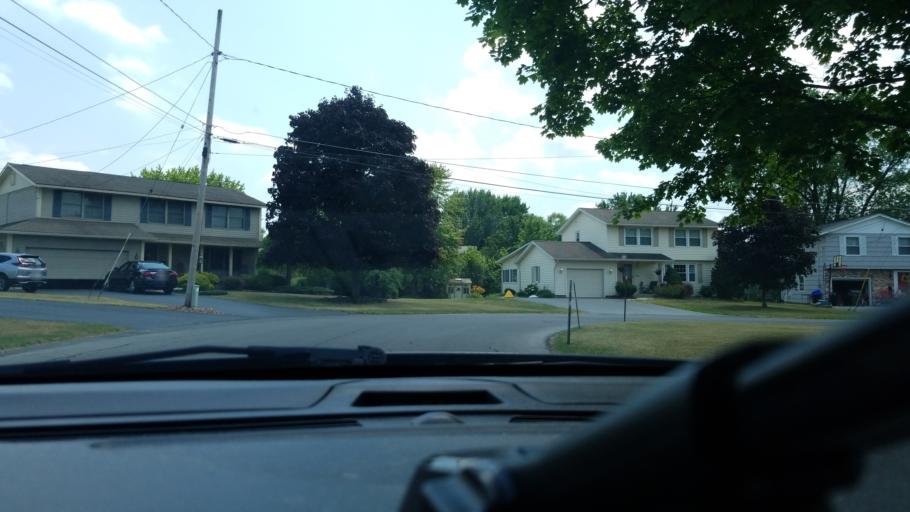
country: US
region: New York
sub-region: Onondaga County
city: Galeville
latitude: 43.1075
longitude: -76.1738
